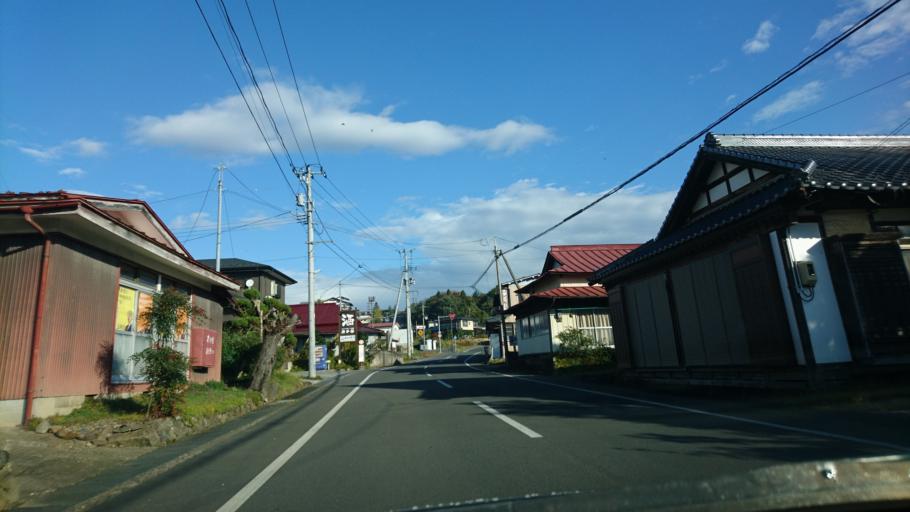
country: JP
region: Iwate
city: Ichinoseki
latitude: 39.0142
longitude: 141.1098
